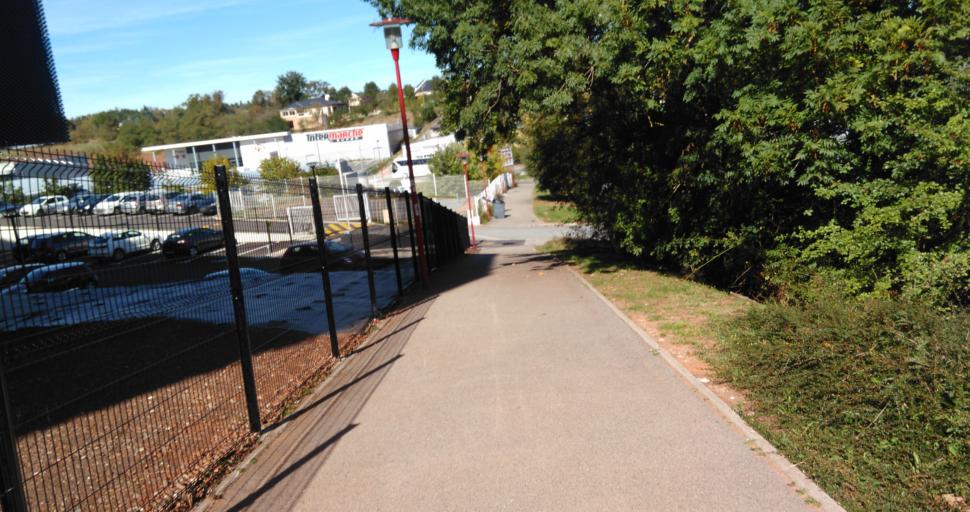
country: FR
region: Midi-Pyrenees
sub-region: Departement de l'Aveyron
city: Olemps
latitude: 44.3621
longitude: 2.5562
